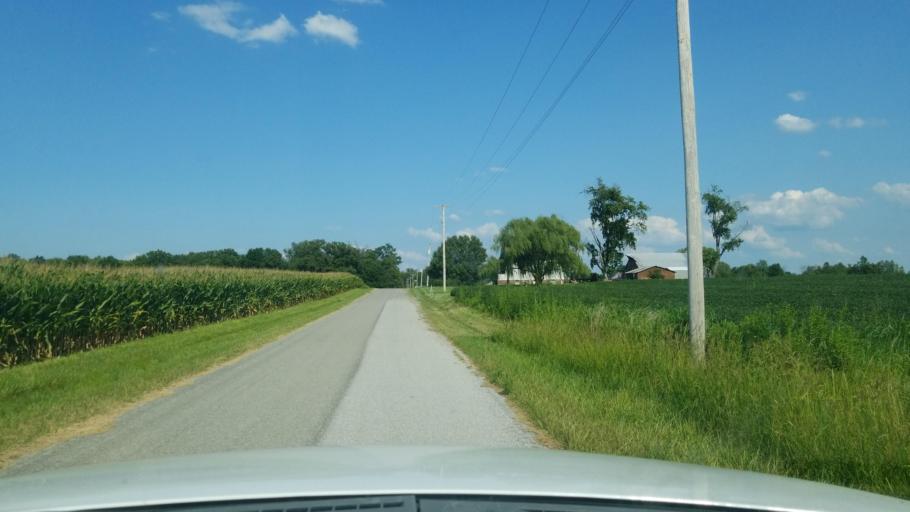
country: US
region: Illinois
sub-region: Saline County
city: Eldorado
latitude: 37.7865
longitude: -88.4959
